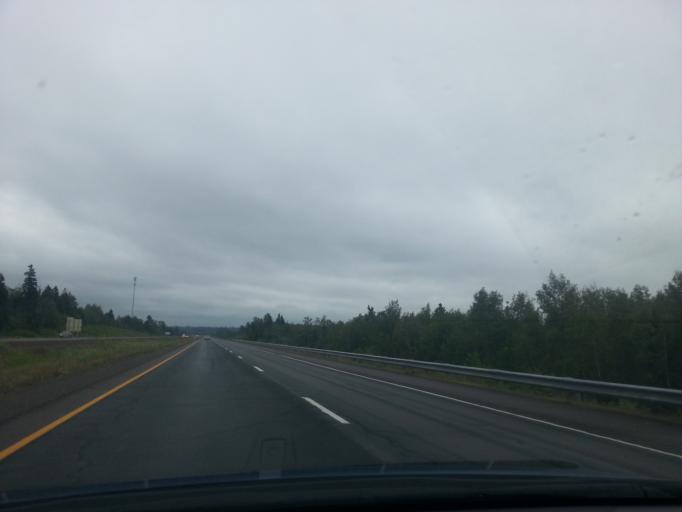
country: CA
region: New Brunswick
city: Fredericton
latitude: 45.8975
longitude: -66.6501
